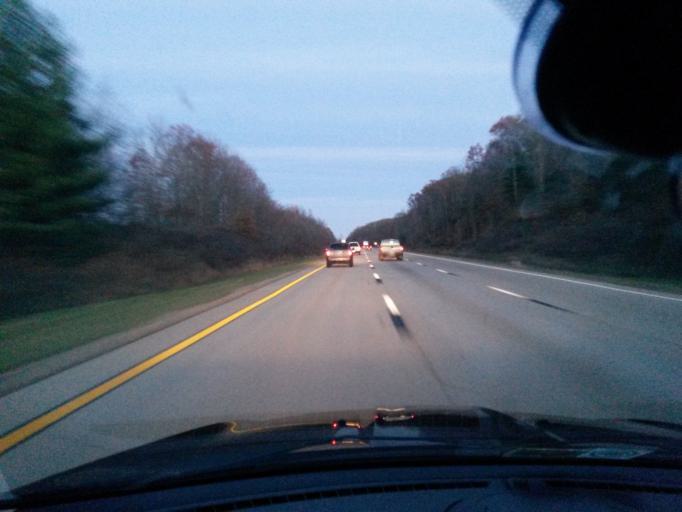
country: US
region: West Virginia
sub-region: Raleigh County
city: Daniels
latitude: 37.7714
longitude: -81.1079
